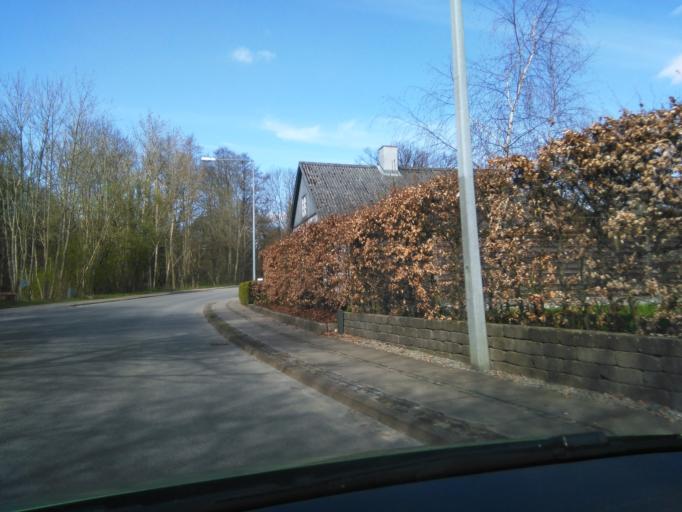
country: DK
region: Central Jutland
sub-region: Odder Kommune
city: Odder
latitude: 55.9834
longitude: 10.1413
